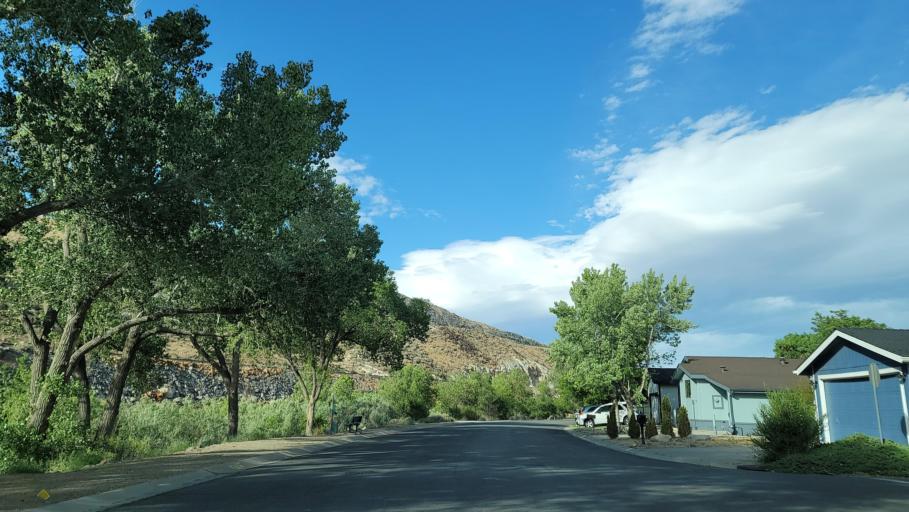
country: US
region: Nevada
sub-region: Washoe County
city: Sparks
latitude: 39.5120
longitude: -119.6441
